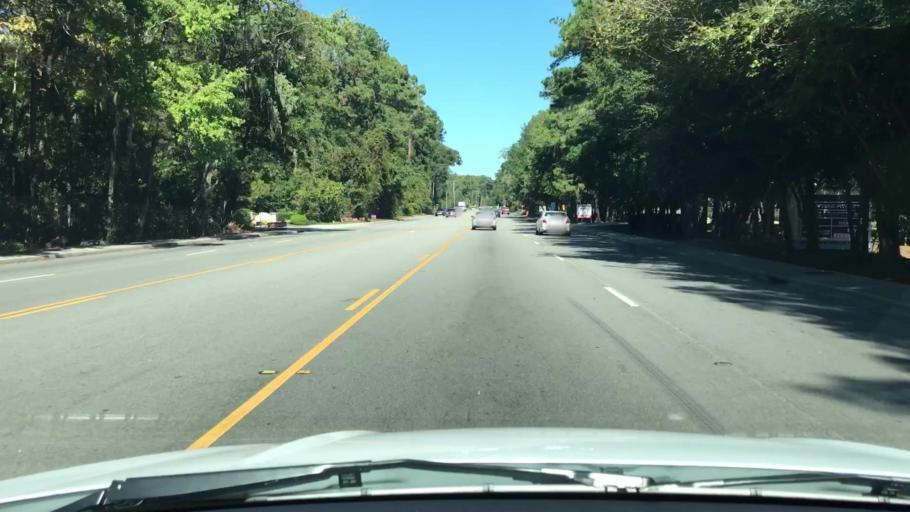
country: US
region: South Carolina
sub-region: Beaufort County
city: Burton
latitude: 32.4279
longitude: -80.7268
